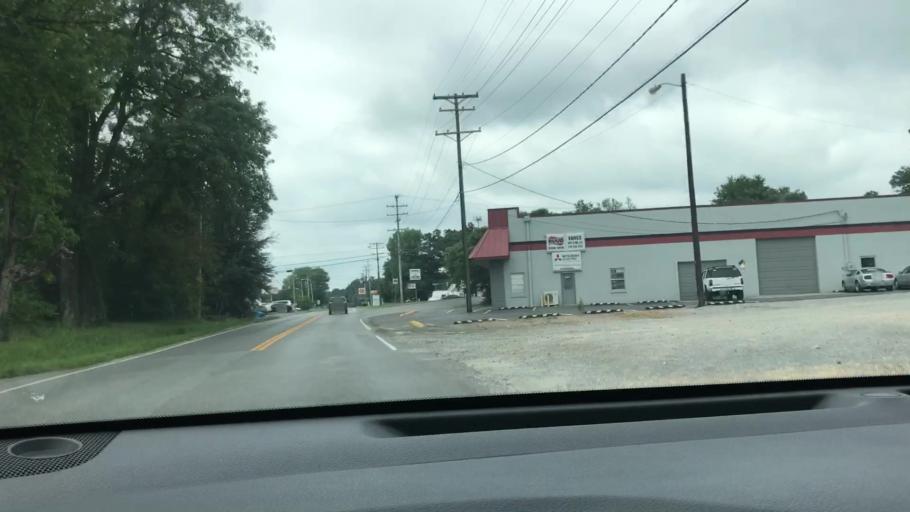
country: US
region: Kentucky
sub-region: Calloway County
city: Murray
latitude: 36.6039
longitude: -88.3024
